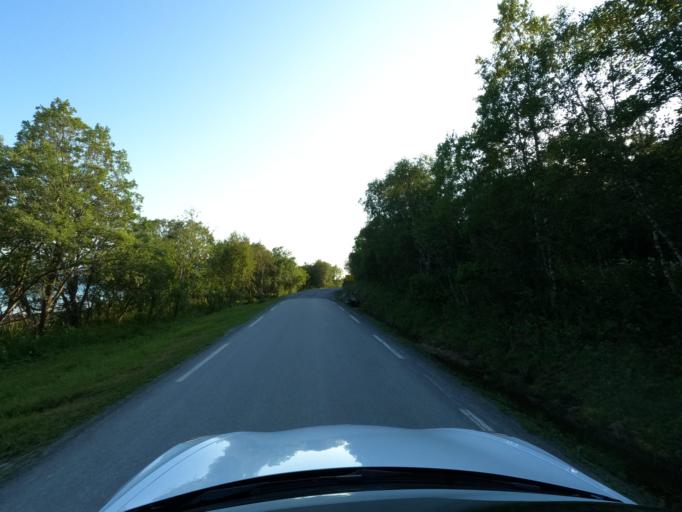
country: NO
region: Nordland
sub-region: Ballangen
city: Ballangen
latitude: 68.4587
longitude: 16.7066
